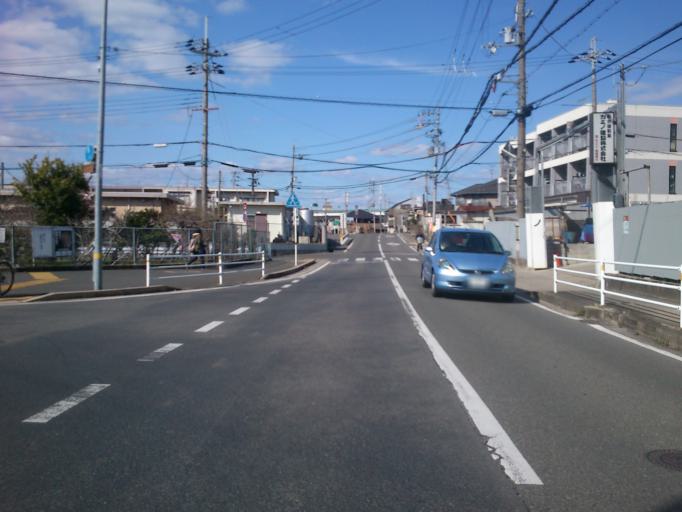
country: JP
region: Kyoto
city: Yawata
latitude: 34.9083
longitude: 135.6888
